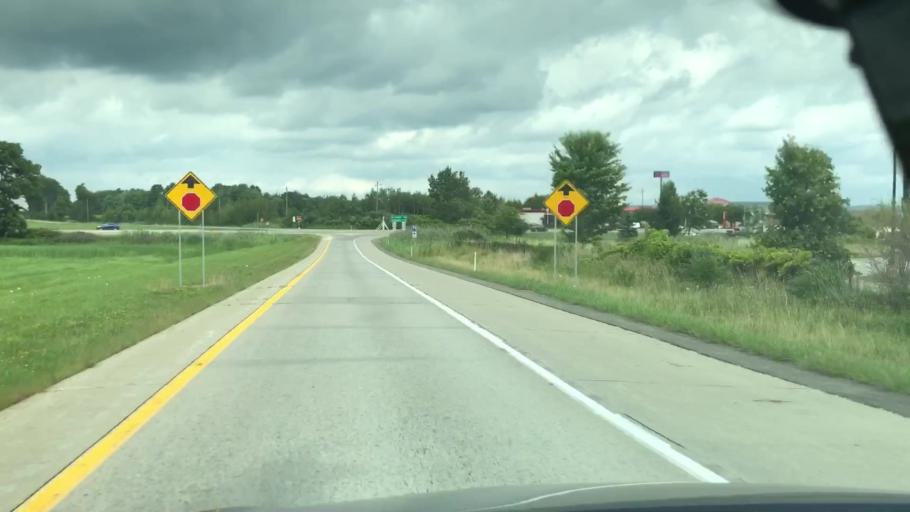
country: US
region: Pennsylvania
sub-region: Erie County
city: Edinboro
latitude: 41.8783
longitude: -80.1755
